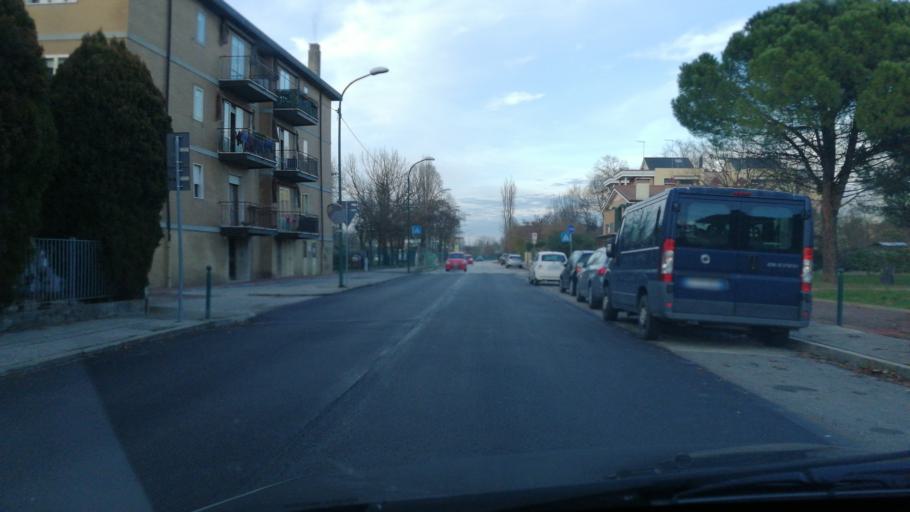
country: IT
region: Veneto
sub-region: Provincia di Venezia
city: Zelarino
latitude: 45.4876
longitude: 12.2103
